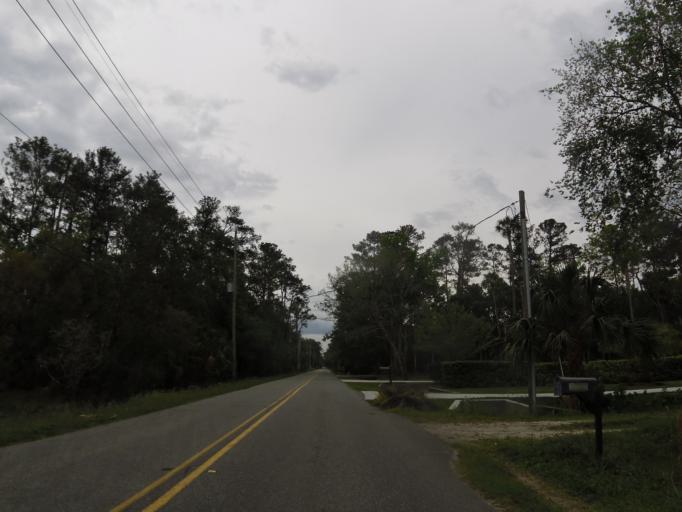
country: US
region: Florida
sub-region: Saint Johns County
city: Palm Valley
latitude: 30.1955
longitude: -81.4050
